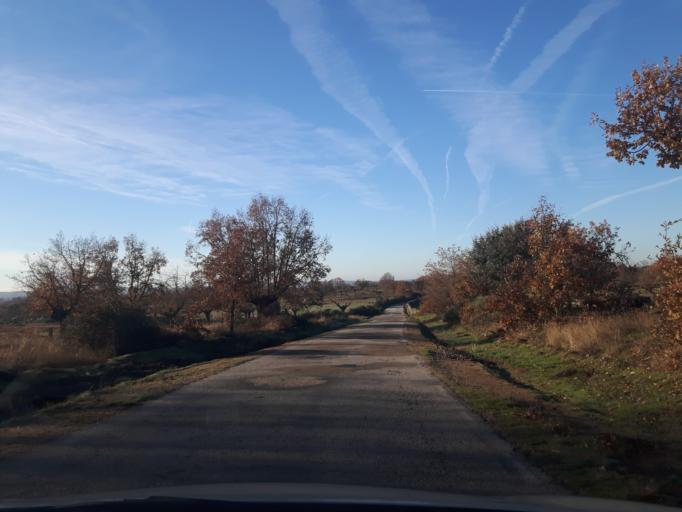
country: ES
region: Castille and Leon
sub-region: Provincia de Salamanca
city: Cerralbo
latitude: 40.9583
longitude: -6.5974
